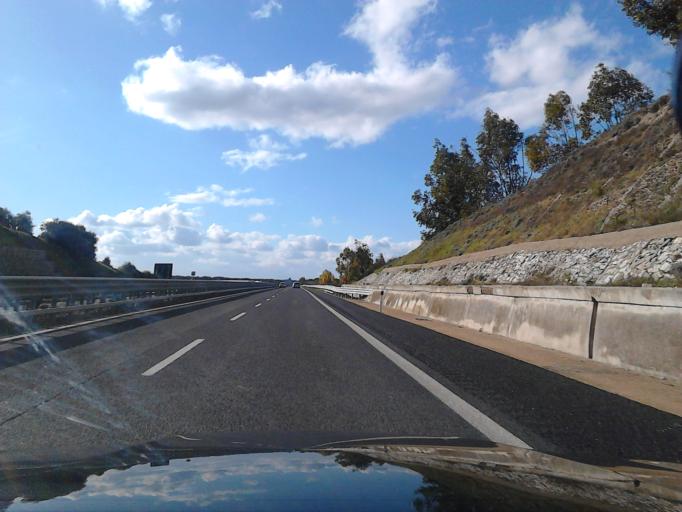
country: IT
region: Apulia
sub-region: Provincia di Barletta - Andria - Trani
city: Canosa di Puglia
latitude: 41.2469
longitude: 16.1678
